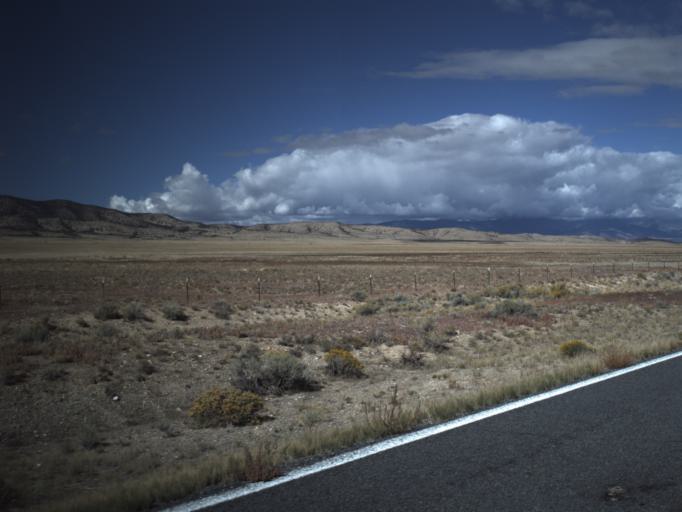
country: US
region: Utah
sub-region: Beaver County
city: Milford
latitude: 38.6543
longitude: -113.8720
